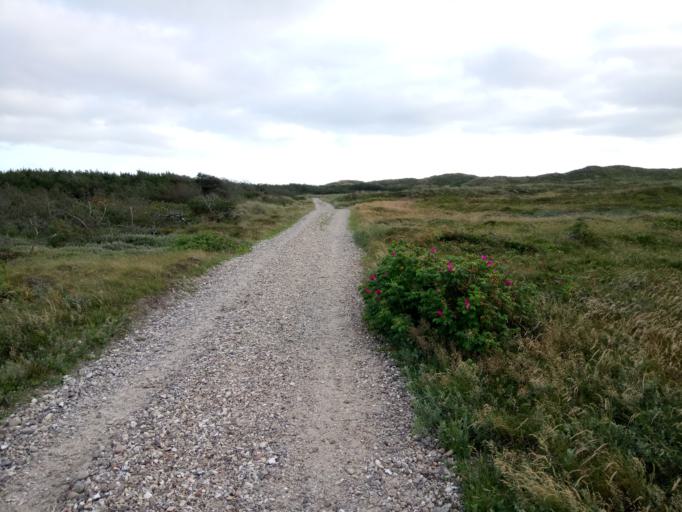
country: DK
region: Central Jutland
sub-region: Holstebro Kommune
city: Ulfborg
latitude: 56.2916
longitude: 8.1341
